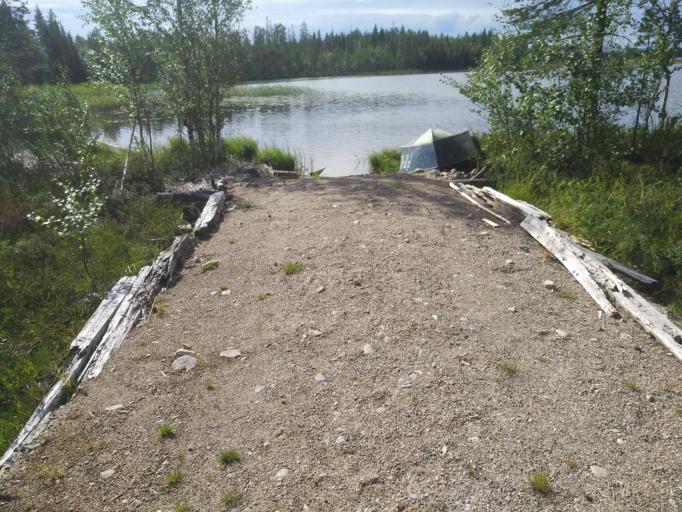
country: RU
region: Republic of Karelia
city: Kalevala
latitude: 64.9855
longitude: 31.2119
